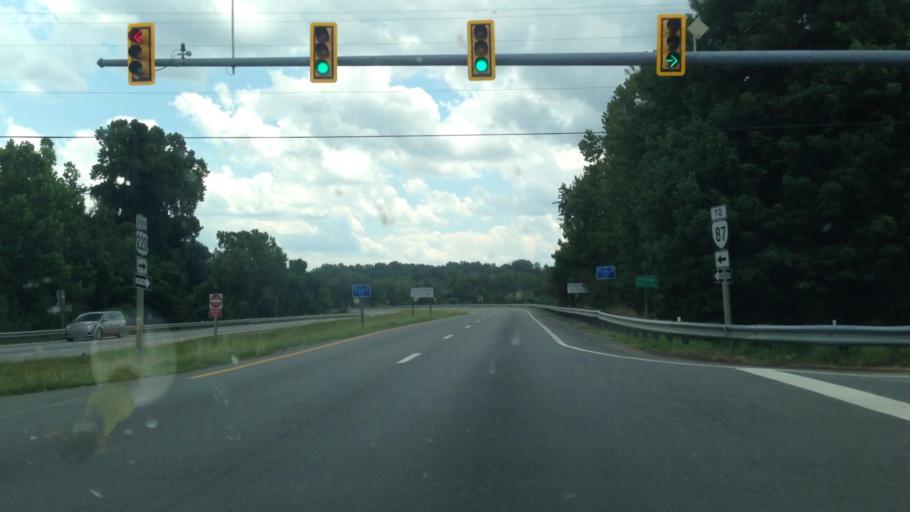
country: US
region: Virginia
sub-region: Henry County
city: Chatmoss
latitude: 36.5872
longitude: -79.8635
